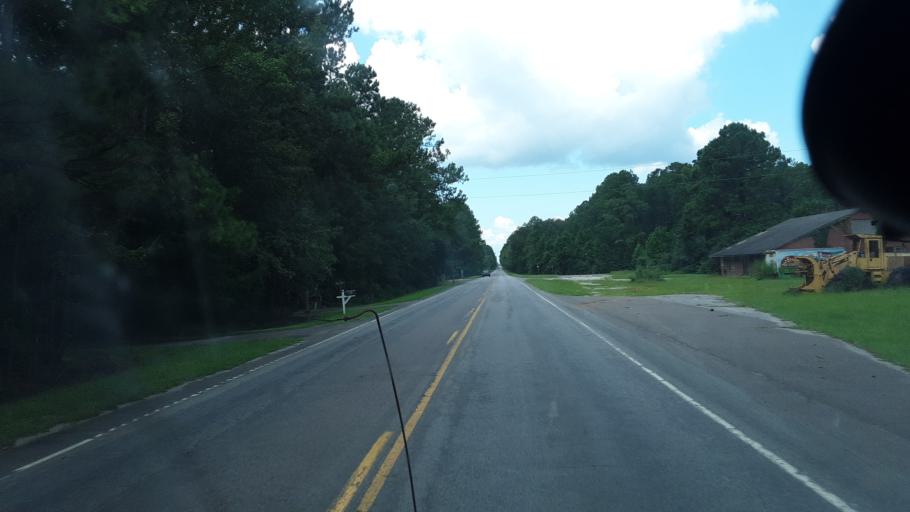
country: US
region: South Carolina
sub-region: Berkeley County
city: Saint Stephen
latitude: 33.2896
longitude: -79.8040
